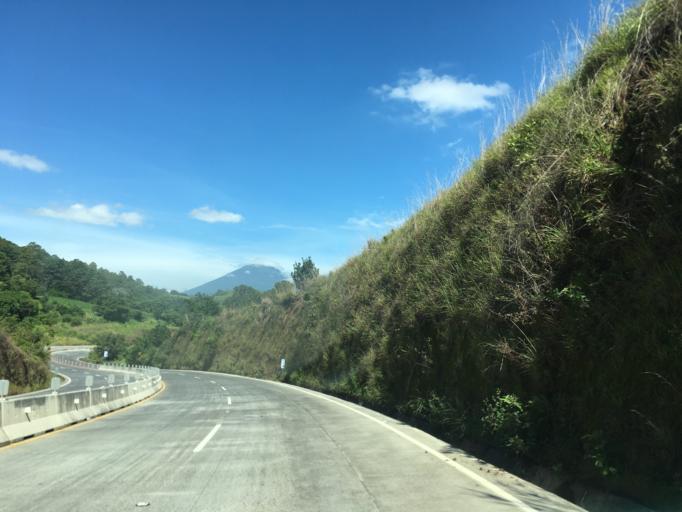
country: GT
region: Guatemala
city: Petapa
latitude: 14.4875
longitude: -90.5508
